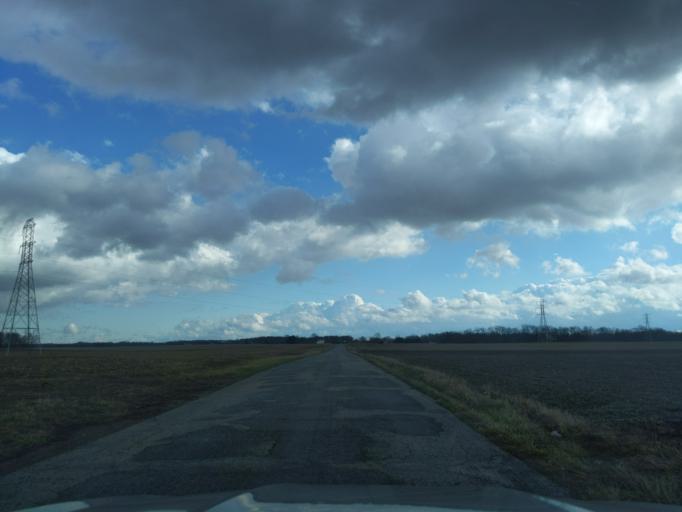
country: US
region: Indiana
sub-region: Decatur County
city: Greensburg
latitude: 39.4092
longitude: -85.5337
